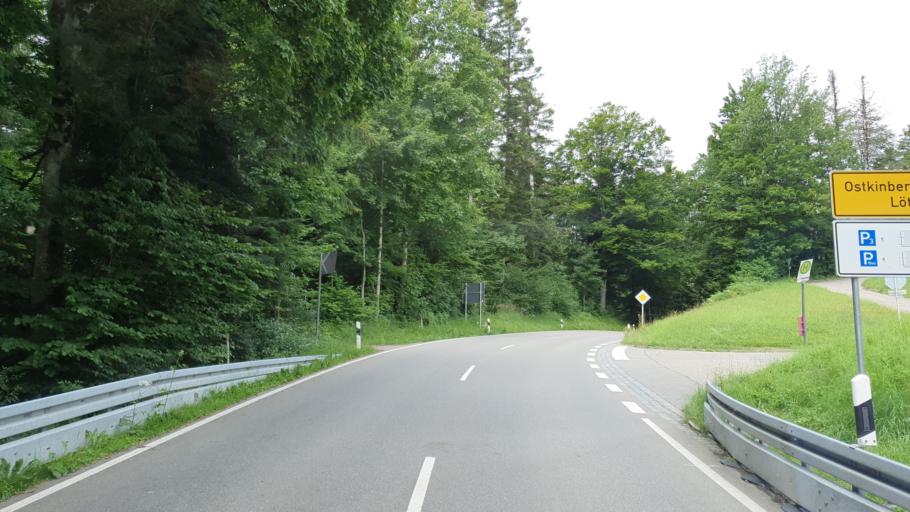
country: DE
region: Bavaria
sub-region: Swabia
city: Scheidegg
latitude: 47.5931
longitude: 9.8398
